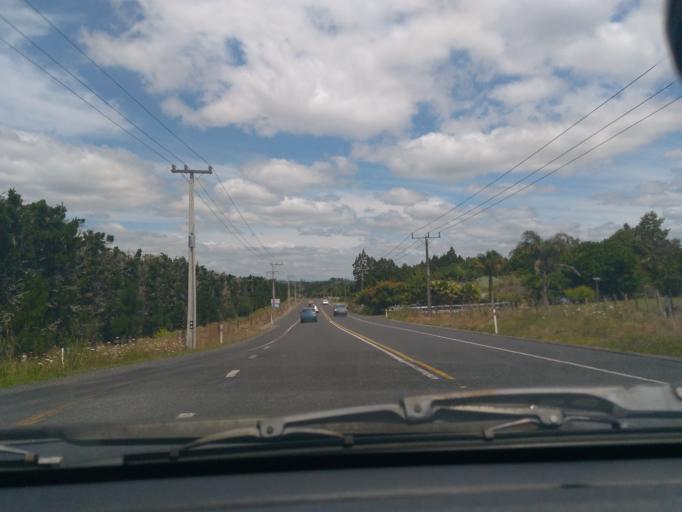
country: NZ
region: Northland
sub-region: Far North District
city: Kerikeri
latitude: -35.1816
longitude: 173.9079
